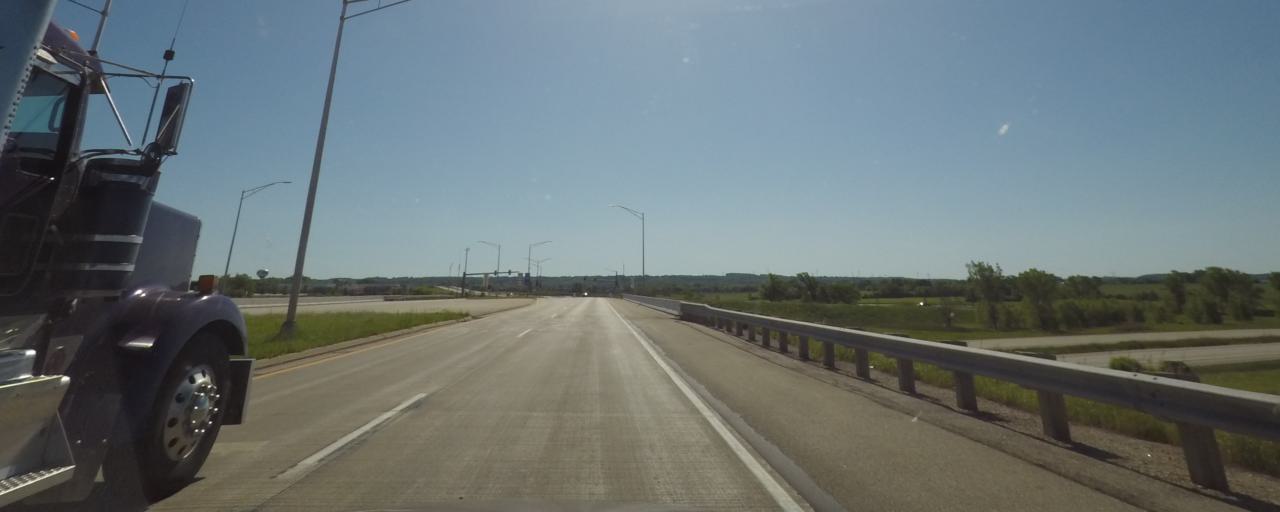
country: US
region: Wisconsin
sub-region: Fond du Lac County
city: Fond du Lac
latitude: 43.7373
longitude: -88.4453
